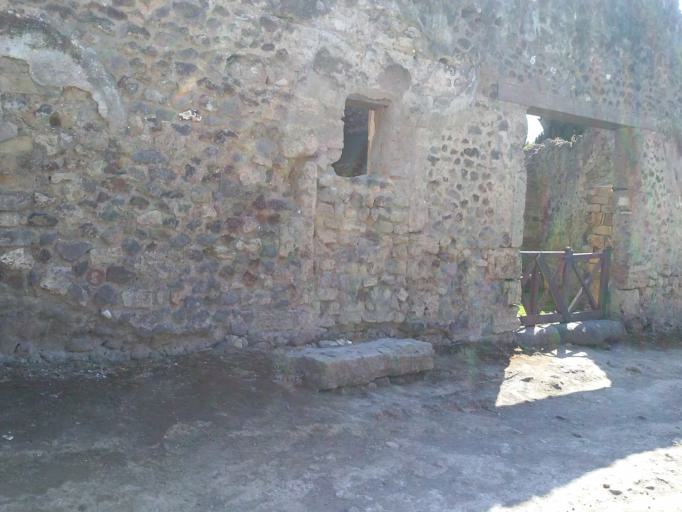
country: IT
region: Campania
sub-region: Provincia di Napoli
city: Pompei
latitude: 40.7525
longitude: 14.4787
